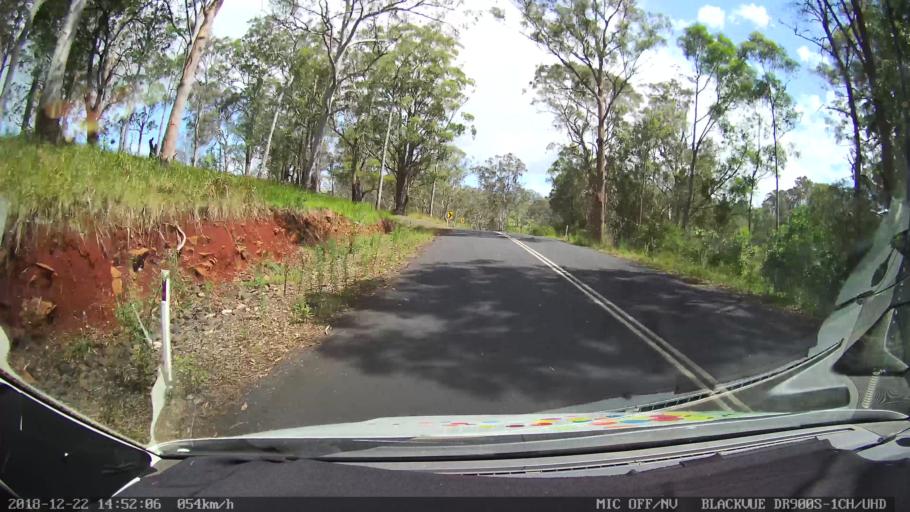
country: AU
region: New South Wales
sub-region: Bellingen
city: Dorrigo
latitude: -30.2071
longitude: 152.5438
